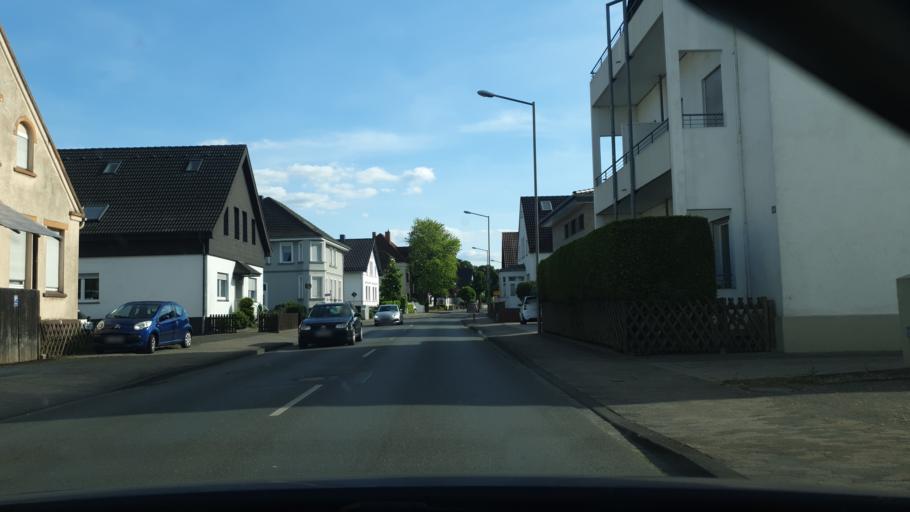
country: DE
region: North Rhine-Westphalia
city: Buende
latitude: 52.1932
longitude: 8.5779
